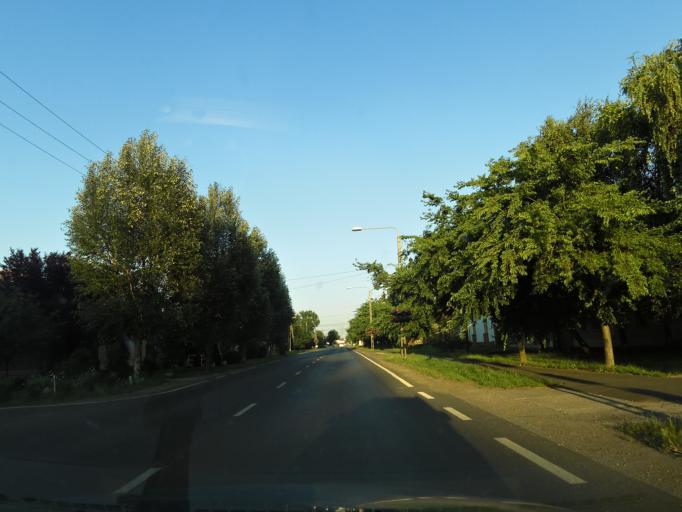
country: HU
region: Csongrad
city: Hodmezovasarhely
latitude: 46.4271
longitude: 20.3316
